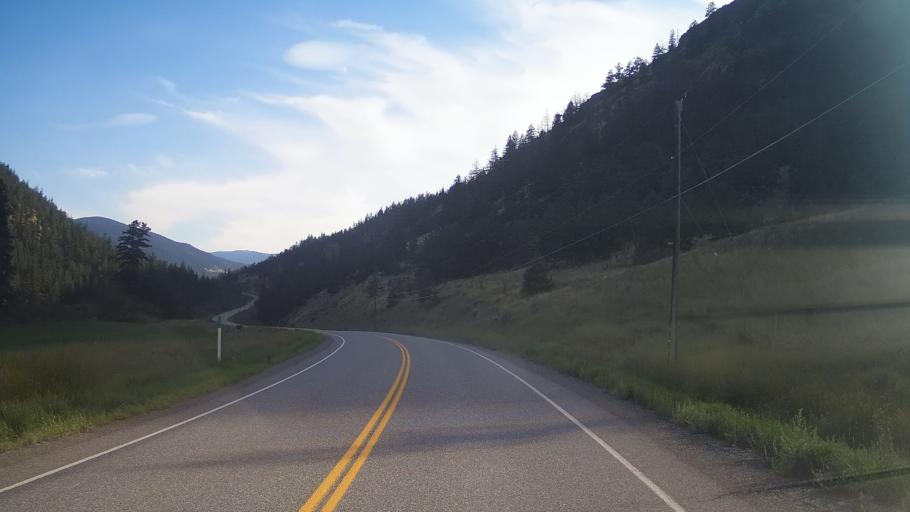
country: CA
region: British Columbia
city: Cache Creek
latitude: 50.8756
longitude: -121.5186
